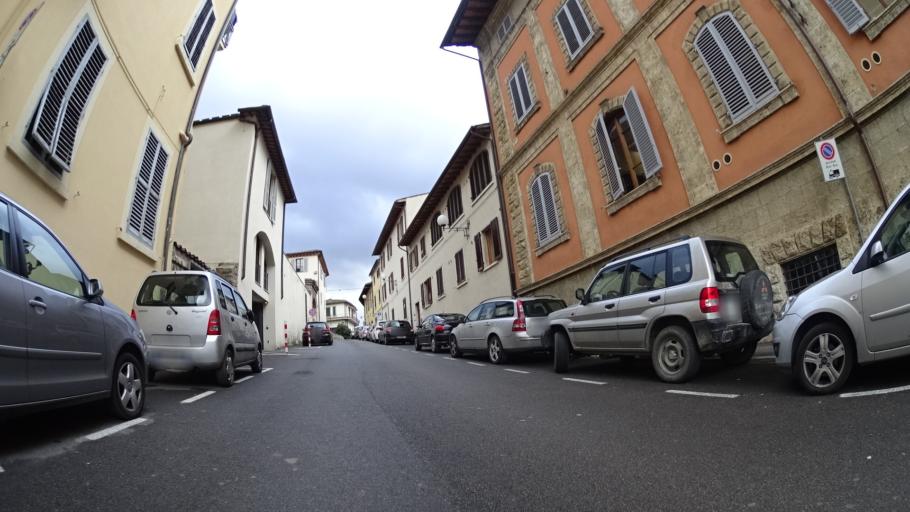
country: IT
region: Tuscany
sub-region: Provincia di Siena
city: Poggibonsi
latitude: 43.4681
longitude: 11.1451
